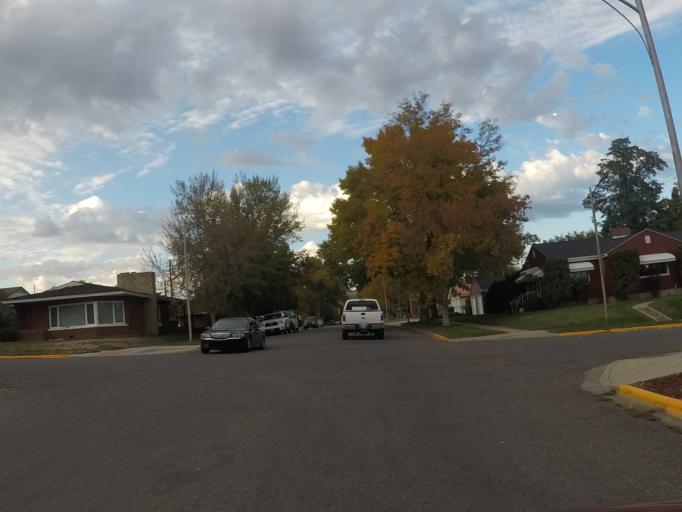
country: US
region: Montana
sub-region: Yellowstone County
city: Billings
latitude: 45.7858
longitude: -108.5306
